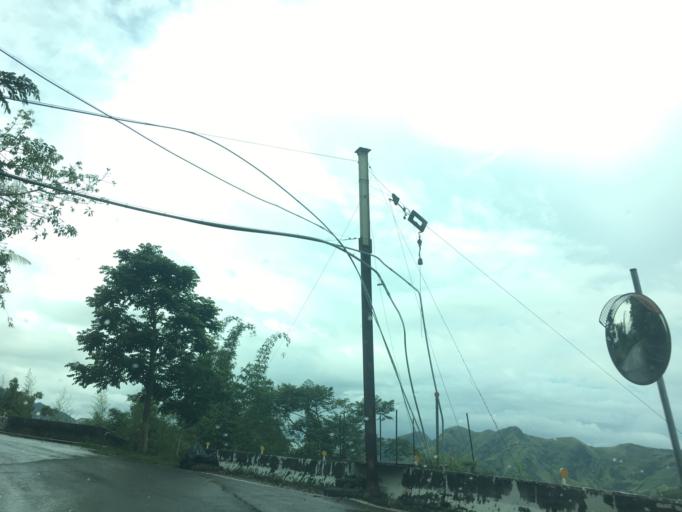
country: TW
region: Taiwan
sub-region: Yunlin
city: Douliu
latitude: 23.5585
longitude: 120.6624
